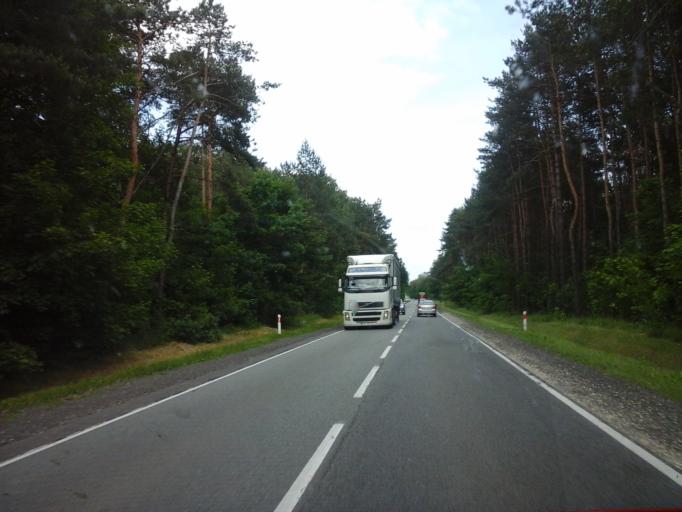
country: PL
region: Lodz Voivodeship
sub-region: Powiat opoczynski
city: Paradyz
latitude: 51.3110
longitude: 20.0876
